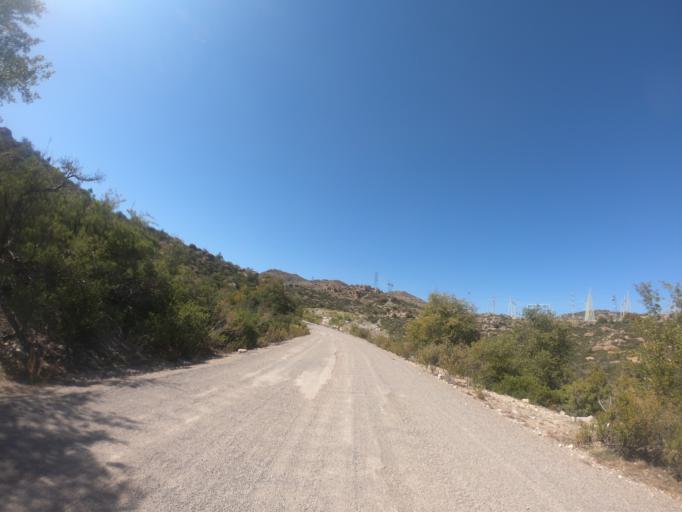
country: US
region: Arizona
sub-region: Pinal County
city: Superior
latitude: 33.3352
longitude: -111.0381
